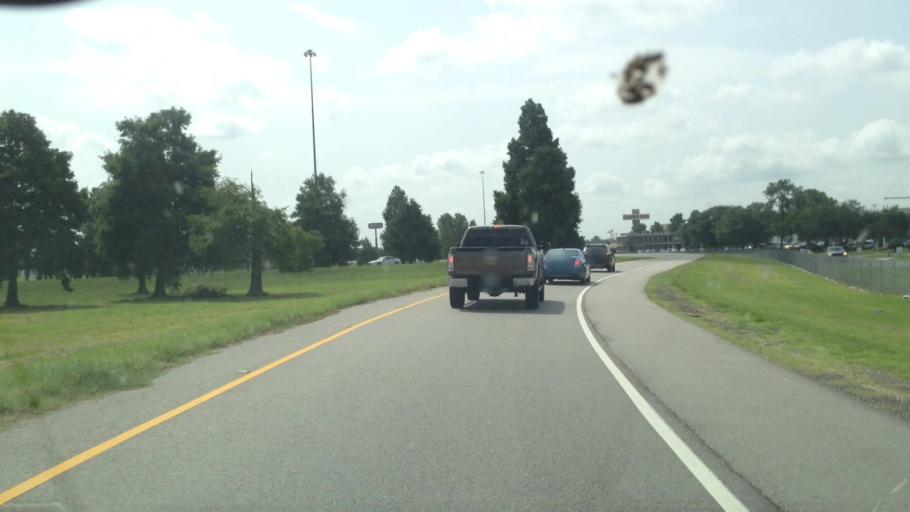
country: US
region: Louisiana
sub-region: Jefferson Parish
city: Metairie Terrace
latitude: 29.9987
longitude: -90.1872
